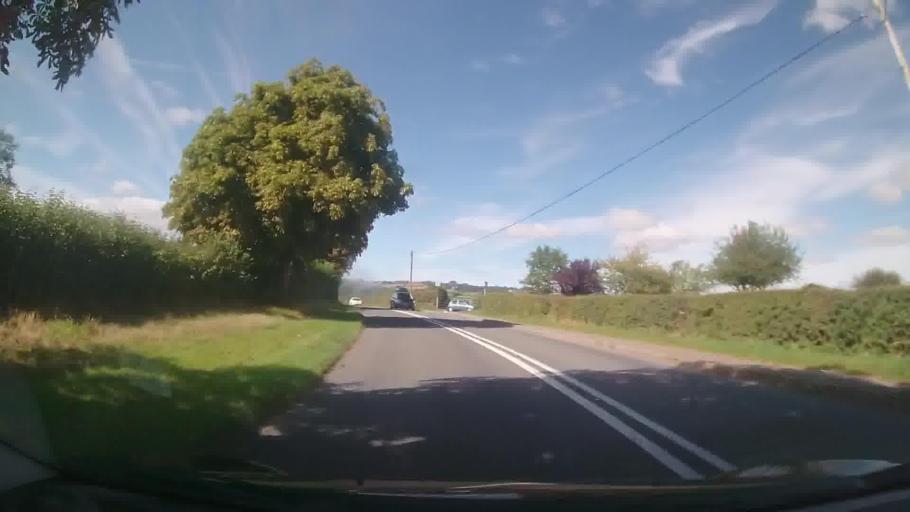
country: GB
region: Wales
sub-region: Sir Powys
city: Hay
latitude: 52.0796
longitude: -3.1330
